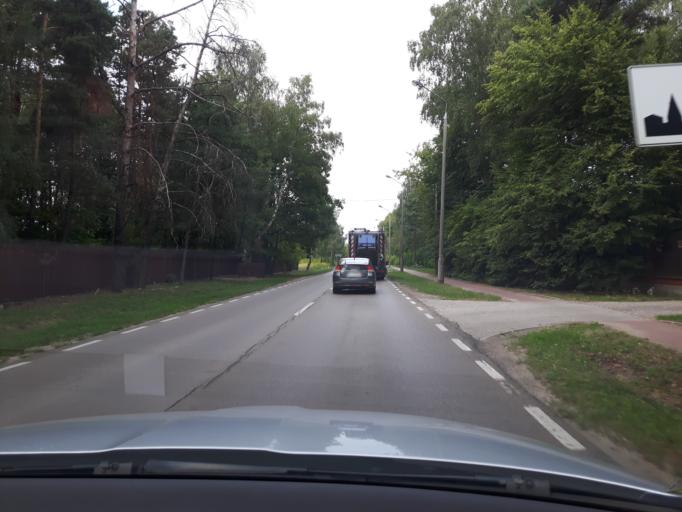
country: PL
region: Masovian Voivodeship
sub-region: Powiat legionowski
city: Stanislawow Pierwszy
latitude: 52.3900
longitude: 21.0321
